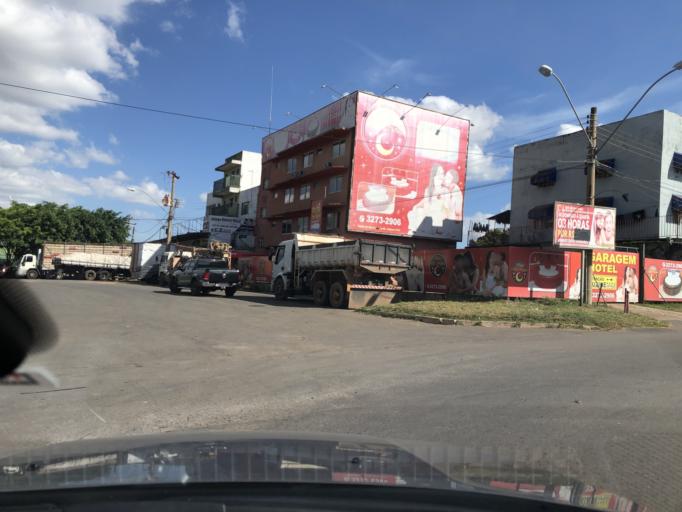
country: BR
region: Federal District
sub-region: Brasilia
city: Brasilia
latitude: -15.7950
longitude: -48.1178
